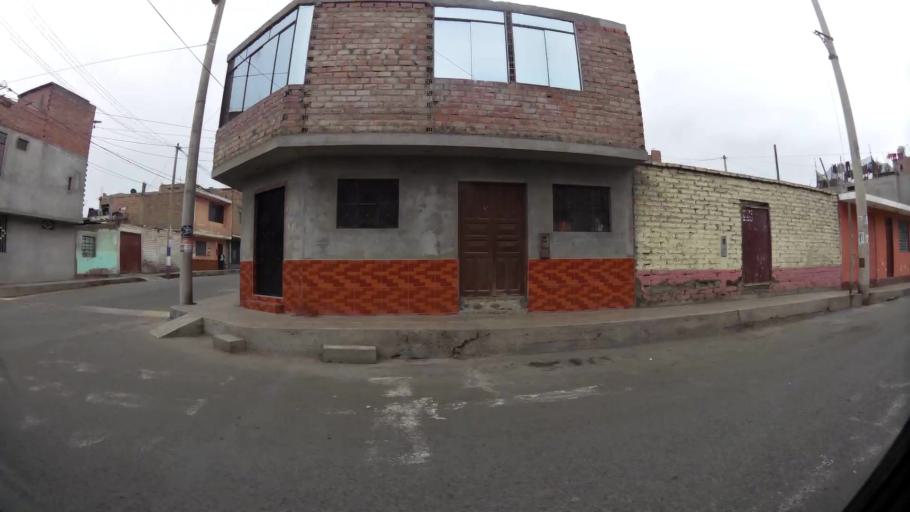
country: PE
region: Lima
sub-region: Barranca
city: Barranca
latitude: -10.7480
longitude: -77.7565
